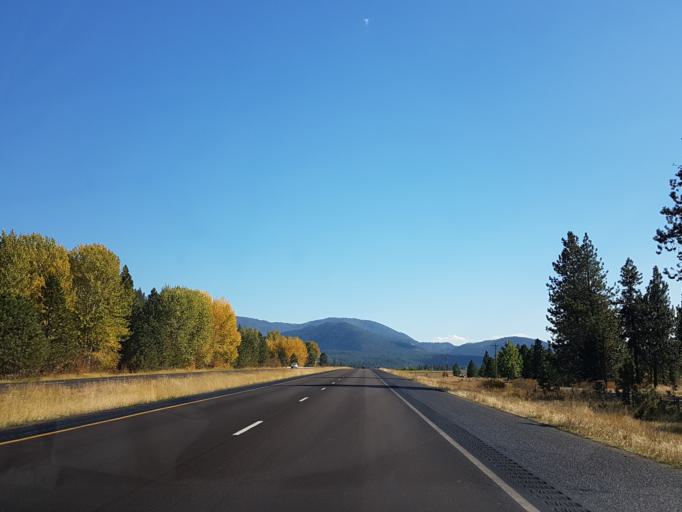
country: US
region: Montana
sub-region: Mineral County
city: Superior
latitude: 47.1445
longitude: -114.8169
